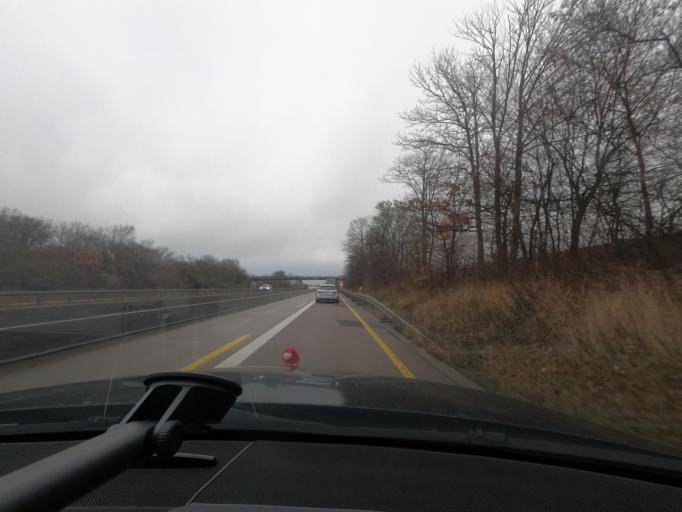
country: DE
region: Lower Saxony
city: Harsum
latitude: 52.2216
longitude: 9.9341
